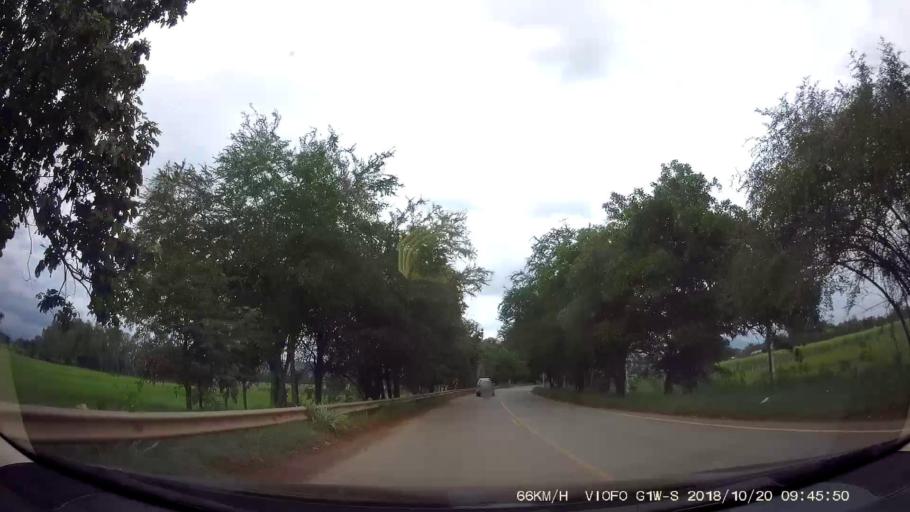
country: TH
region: Chaiyaphum
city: Khon San
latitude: 16.4918
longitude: 101.9316
